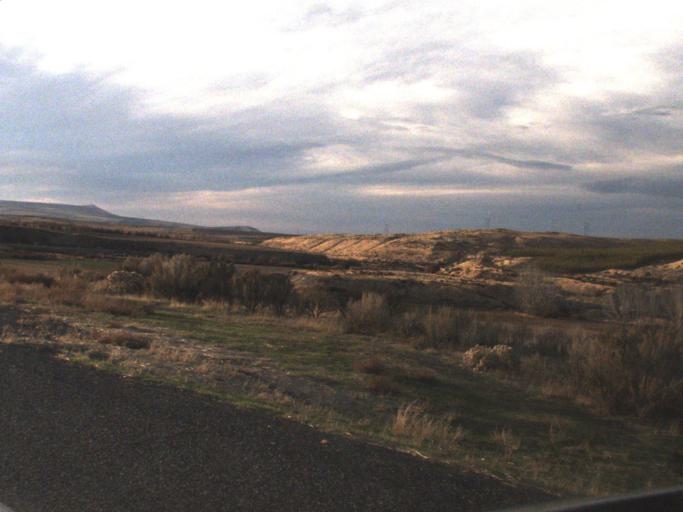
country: US
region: Washington
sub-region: Benton County
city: Finley
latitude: 46.0699
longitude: -118.8176
